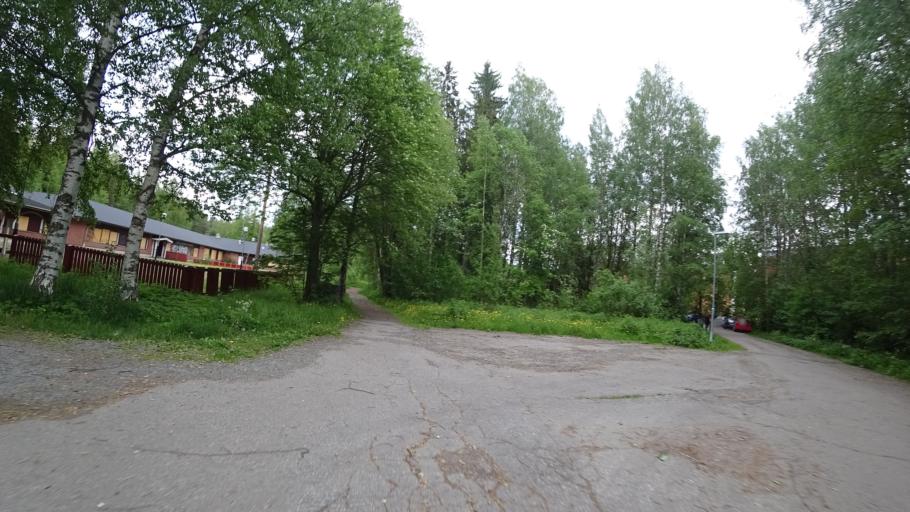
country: FI
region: Pirkanmaa
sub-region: Tampere
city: Yloejaervi
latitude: 61.5184
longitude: 23.6046
